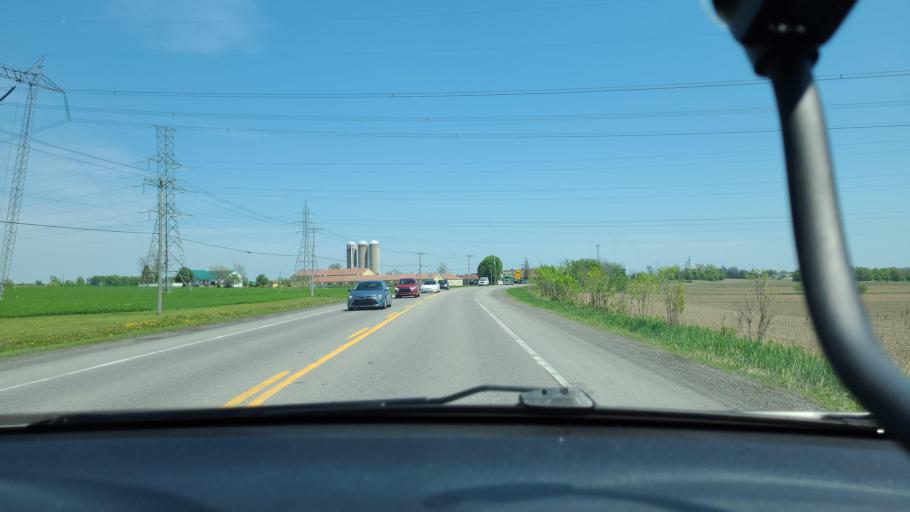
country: CA
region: Quebec
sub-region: Laurentides
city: Mirabel
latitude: 45.6010
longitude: -74.0473
